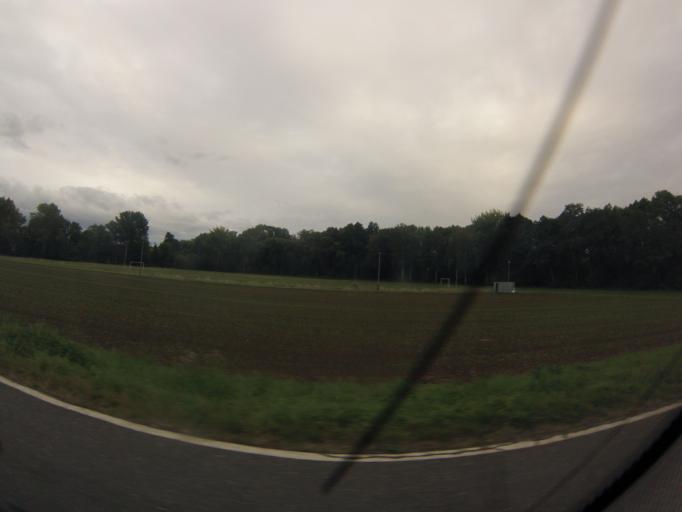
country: DE
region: Thuringia
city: Nobdenitz
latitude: 50.8795
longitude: 12.2863
